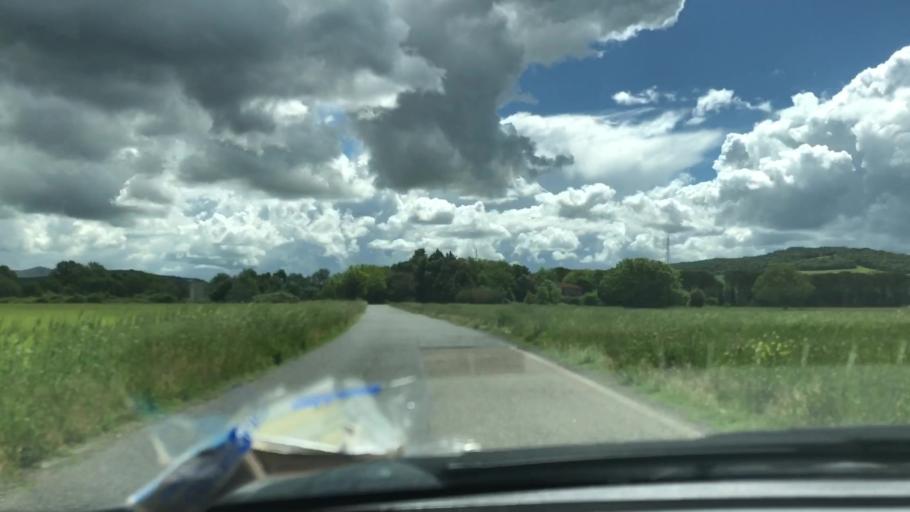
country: IT
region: Tuscany
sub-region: Province of Pisa
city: Saline
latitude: 43.3510
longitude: 10.7894
